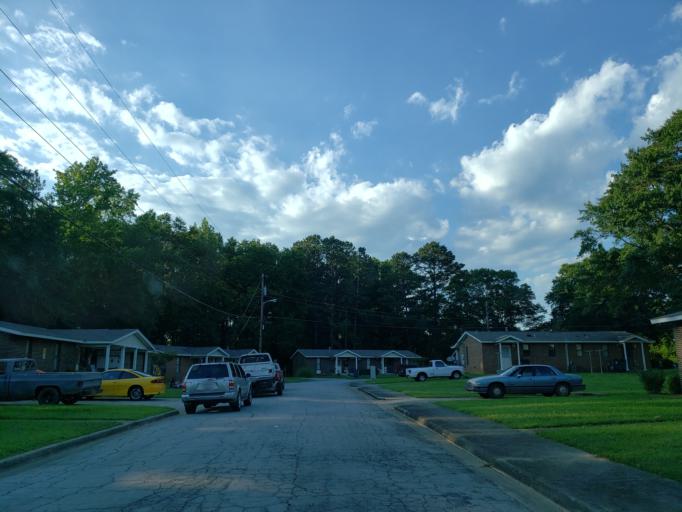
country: US
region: Georgia
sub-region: Haralson County
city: Tallapoosa
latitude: 33.7520
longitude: -85.2983
